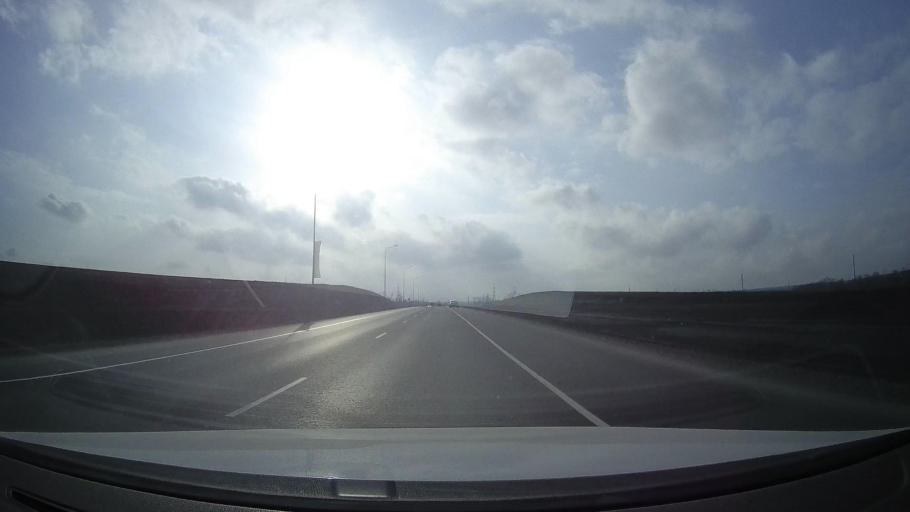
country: RU
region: Rostov
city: Grushevskaya
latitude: 47.4167
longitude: 39.8611
